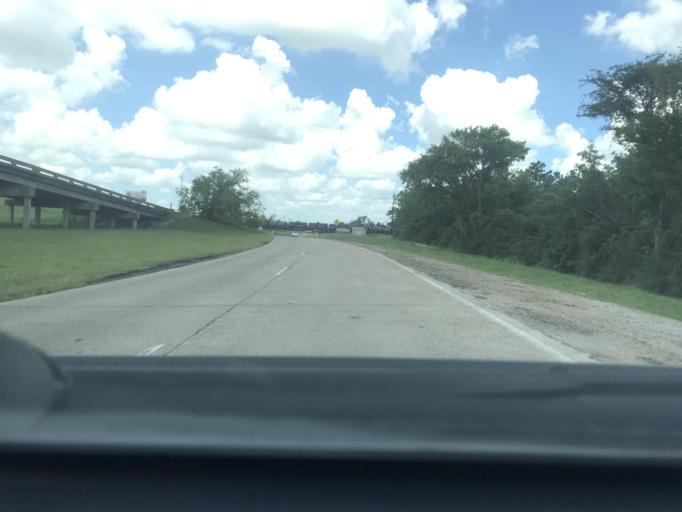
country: US
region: Louisiana
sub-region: Calcasieu Parish
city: Westlake
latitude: 30.2375
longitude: -93.2801
